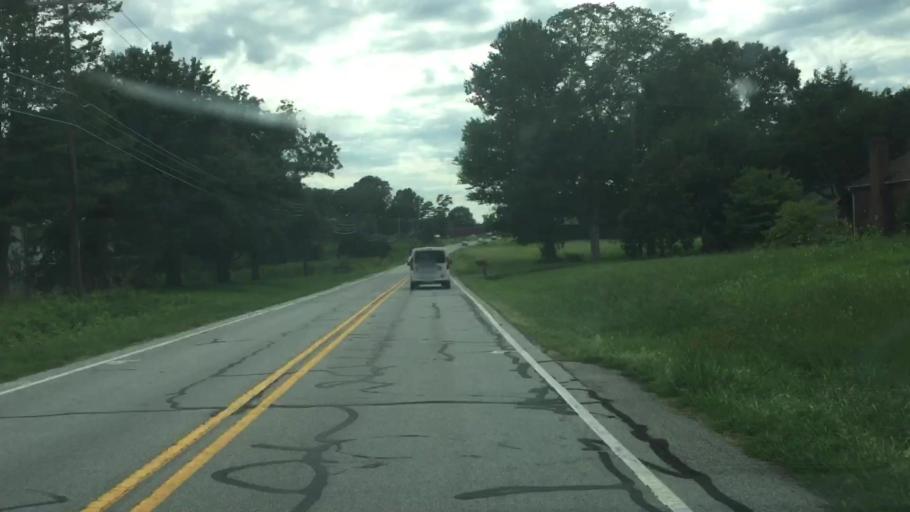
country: US
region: North Carolina
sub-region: Rowan County
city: China Grove
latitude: 35.6584
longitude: -80.5680
